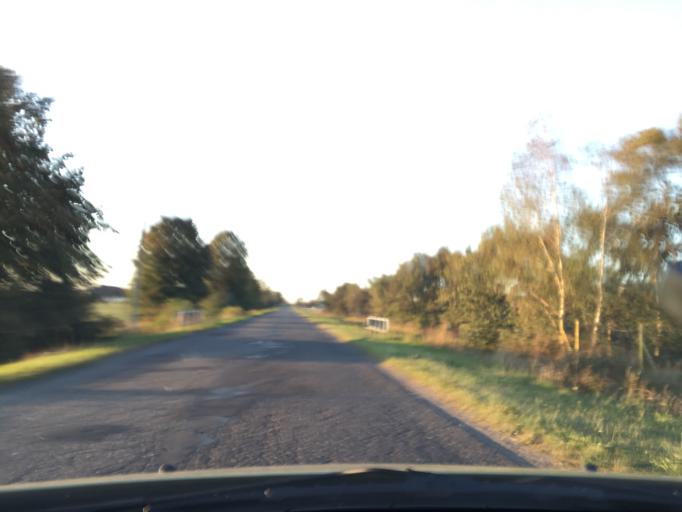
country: PL
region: Greater Poland Voivodeship
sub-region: Powiat pleszewski
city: Dobrzyca
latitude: 51.8237
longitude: 17.6204
